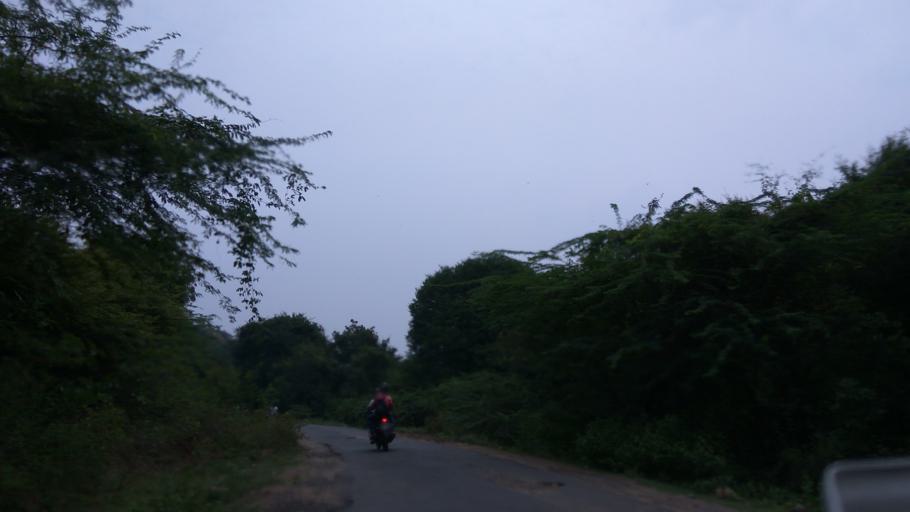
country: IN
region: Tamil Nadu
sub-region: Dharmapuri
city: Dharmapuri
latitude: 12.0132
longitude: 78.1295
